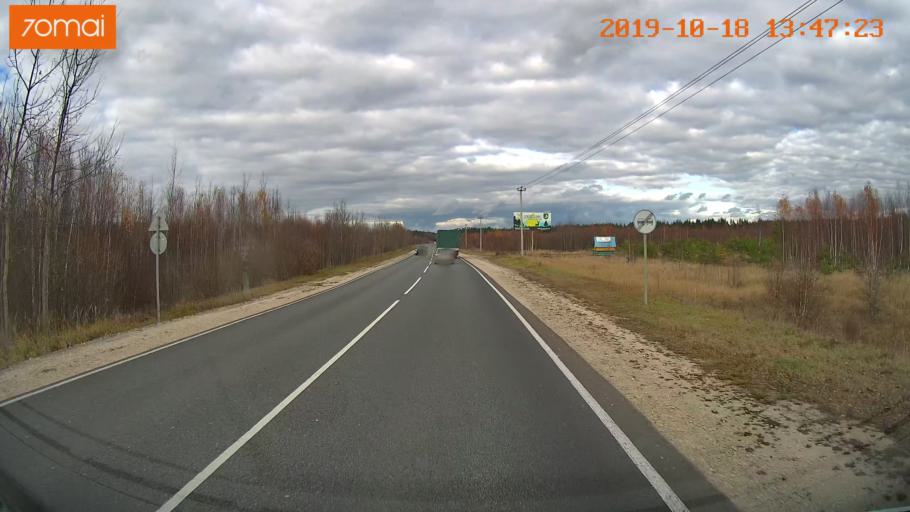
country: RU
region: Rjazan
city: Solotcha
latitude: 54.9738
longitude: 39.9512
